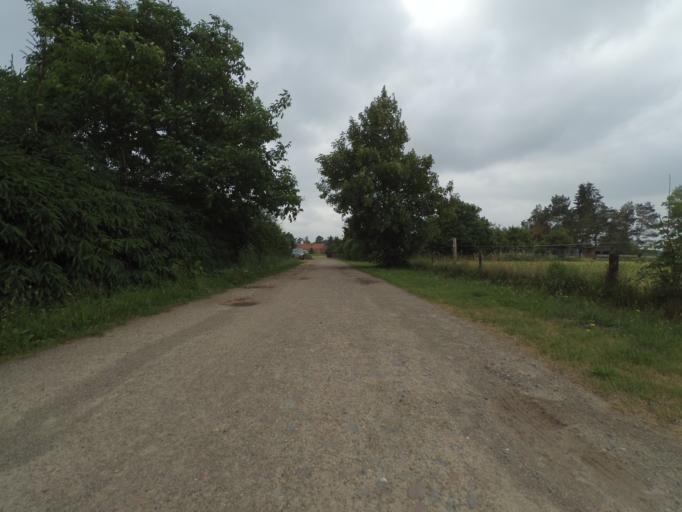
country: DE
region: Mecklenburg-Vorpommern
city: Neustadt-Glewe
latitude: 53.4112
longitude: 11.5738
